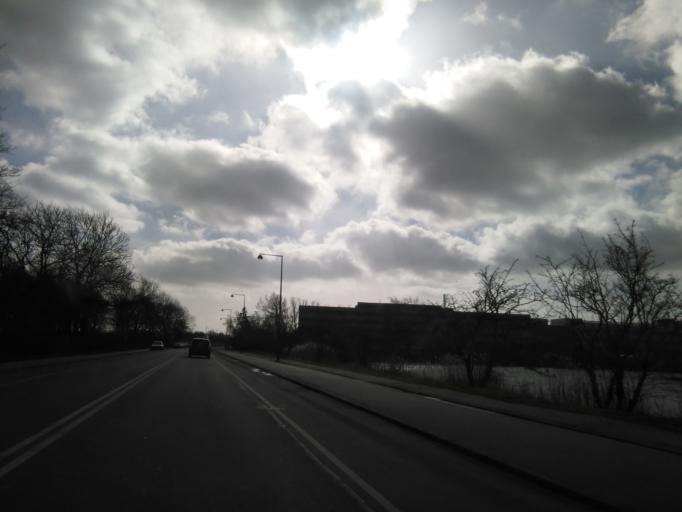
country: DK
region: Capital Region
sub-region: Tarnby Kommune
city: Tarnby
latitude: 55.6480
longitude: 12.6422
